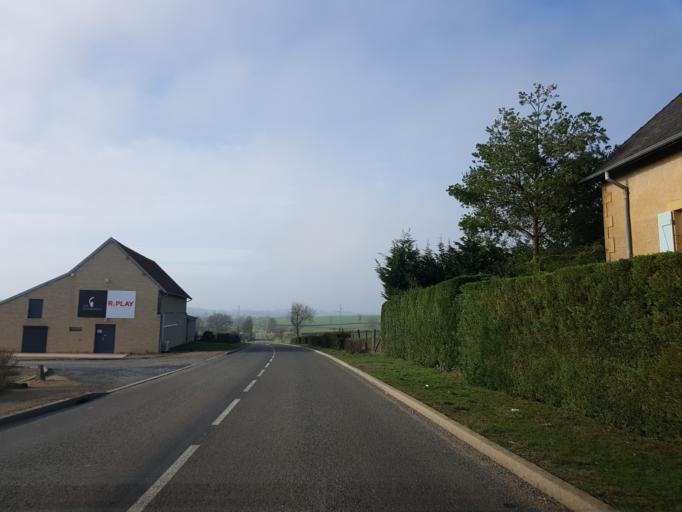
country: FR
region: Bourgogne
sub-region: Departement de Saone-et-Loire
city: Gueugnon
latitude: 46.5980
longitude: 3.9938
